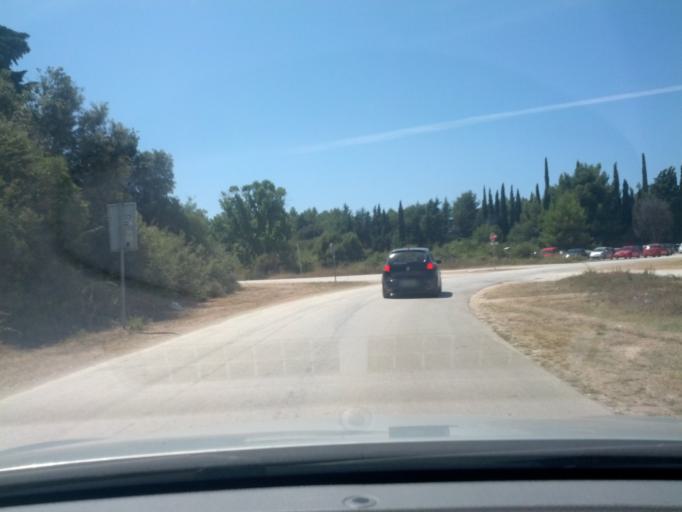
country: HR
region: Istarska
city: Fazana
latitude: 44.8986
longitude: 13.8101
